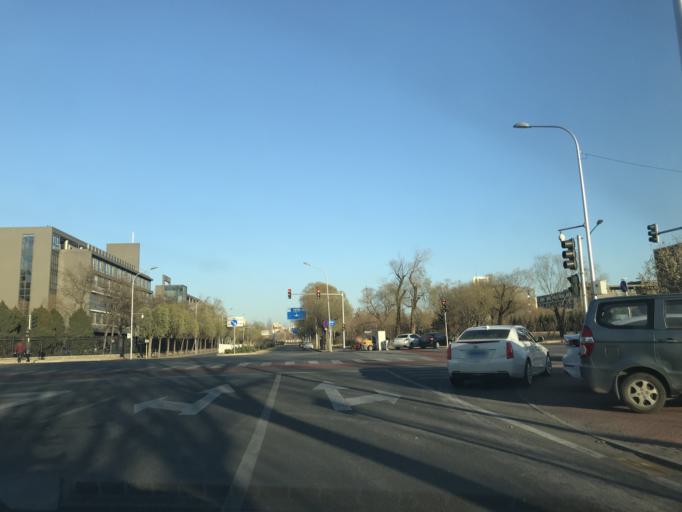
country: CN
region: Beijing
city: Xibeiwang
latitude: 40.0718
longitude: 116.2452
